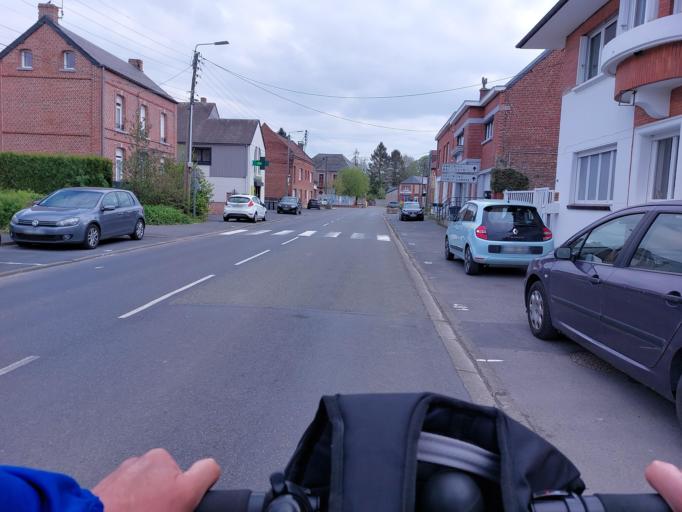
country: FR
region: Nord-Pas-de-Calais
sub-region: Departement du Nord
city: La Longueville
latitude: 50.2903
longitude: 3.8552
